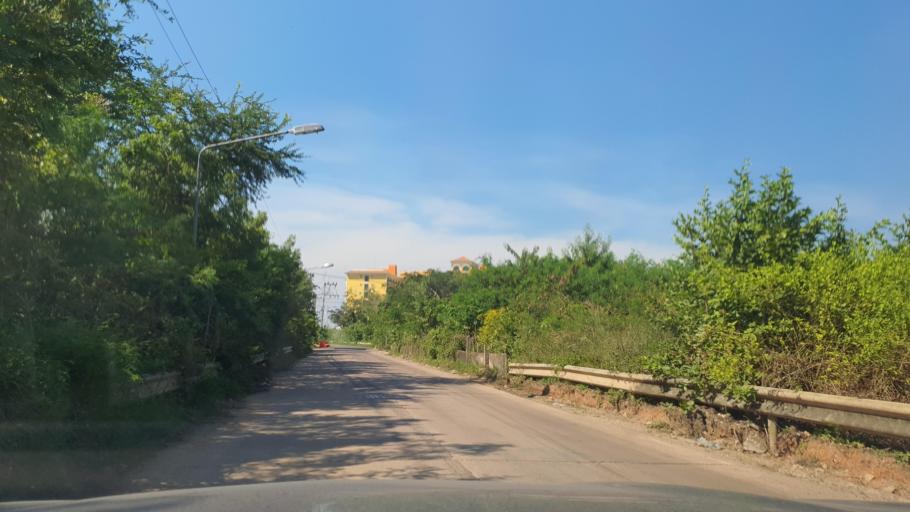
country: TH
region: Chon Buri
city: Phatthaya
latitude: 12.8610
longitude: 100.9032
